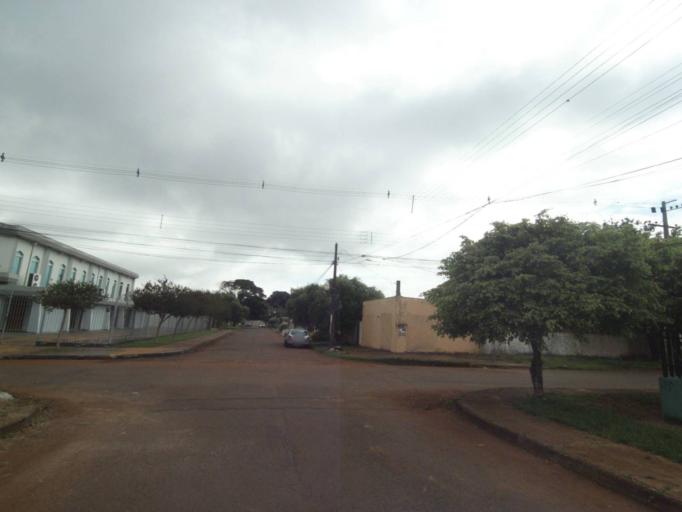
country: BR
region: Parana
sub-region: Campo Mourao
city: Campo Mourao
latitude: -24.0219
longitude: -52.3594
